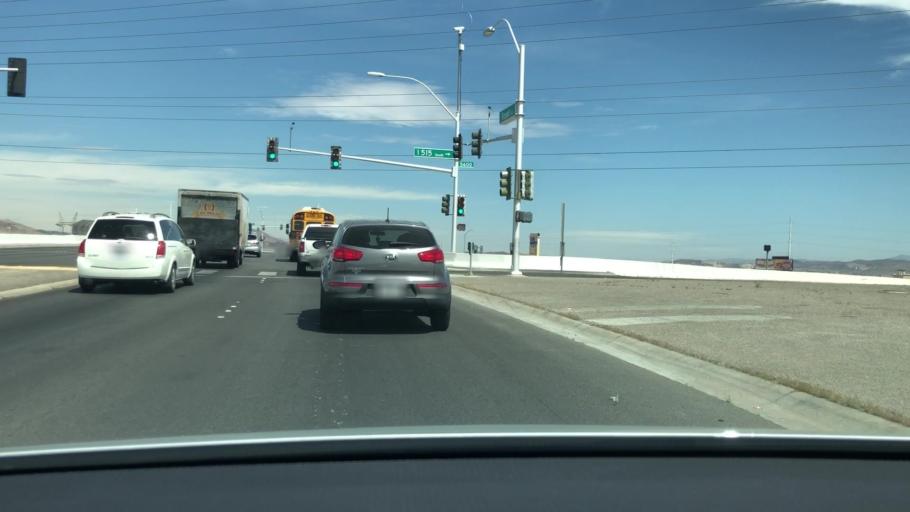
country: US
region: Nevada
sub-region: Clark County
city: Whitney
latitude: 36.0825
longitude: -115.0510
